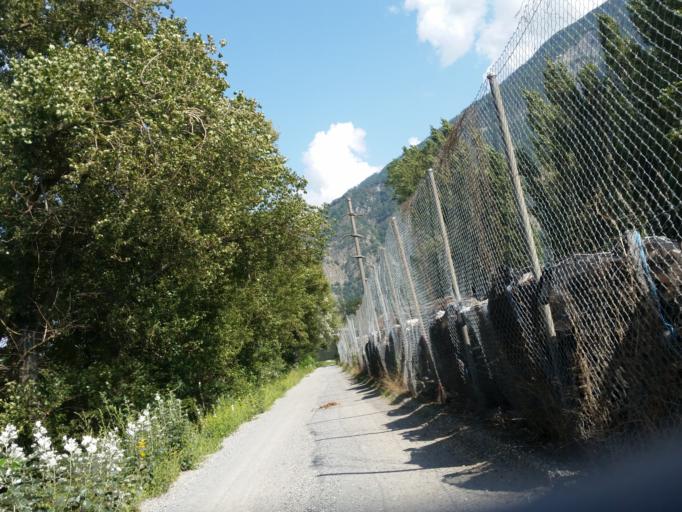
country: CH
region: Valais
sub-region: Martigny District
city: Riddes
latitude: 46.1779
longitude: 7.2200
